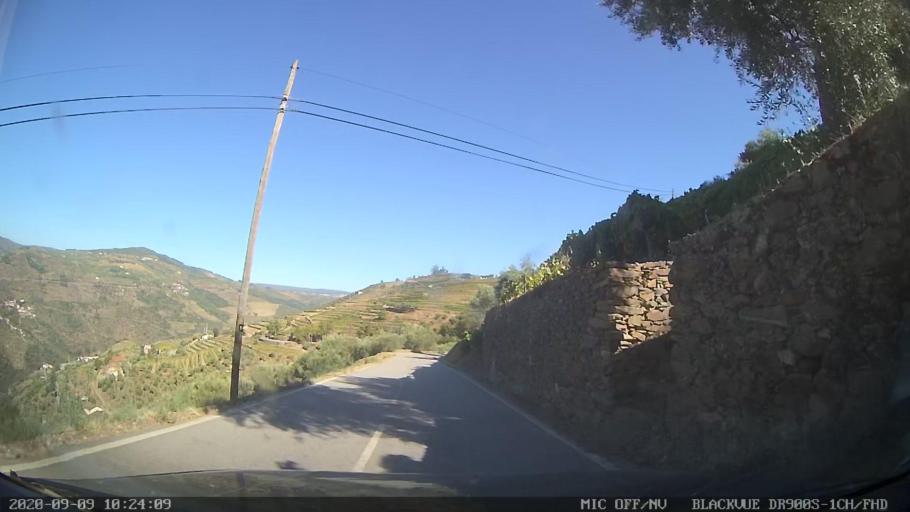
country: PT
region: Vila Real
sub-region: Sabrosa
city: Vilela
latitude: 41.2030
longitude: -7.5287
